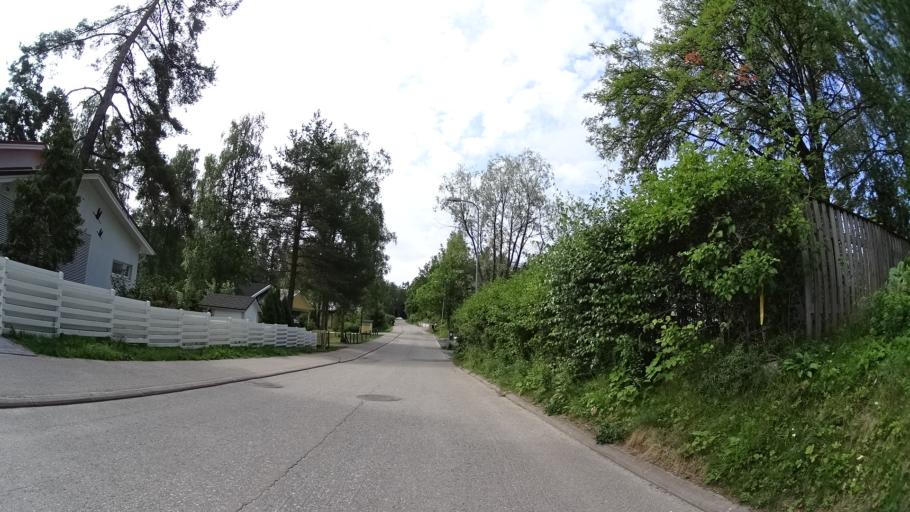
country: FI
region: Uusimaa
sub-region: Helsinki
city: Espoo
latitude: 60.2018
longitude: 24.6062
